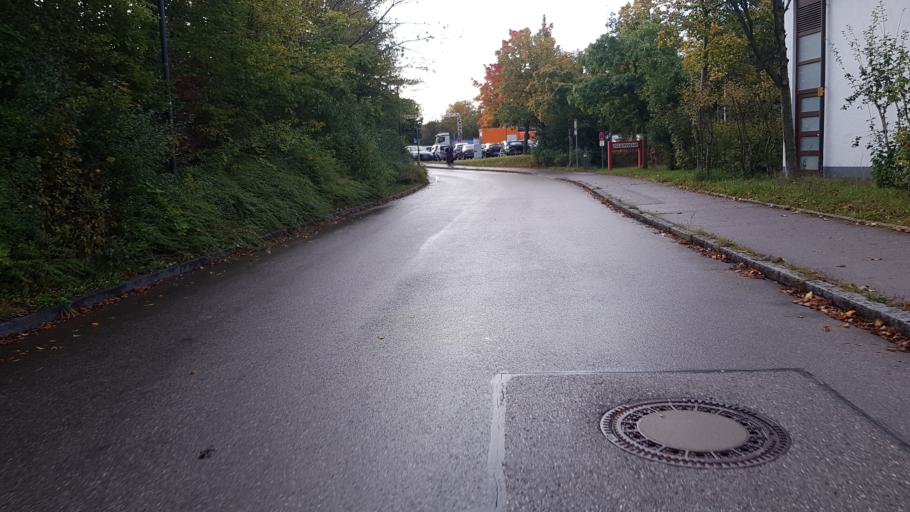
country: DE
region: Bavaria
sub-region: Upper Bavaria
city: Neubiberg
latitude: 48.0780
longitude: 11.6581
